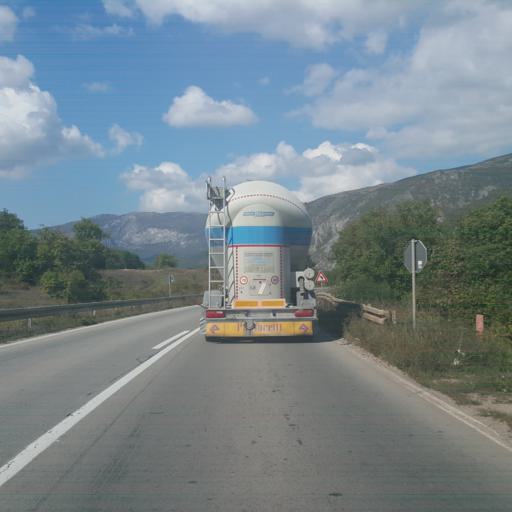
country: RS
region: Central Serbia
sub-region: Pirotski Okrug
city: Bela Palanka
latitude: 43.2850
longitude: 22.2198
